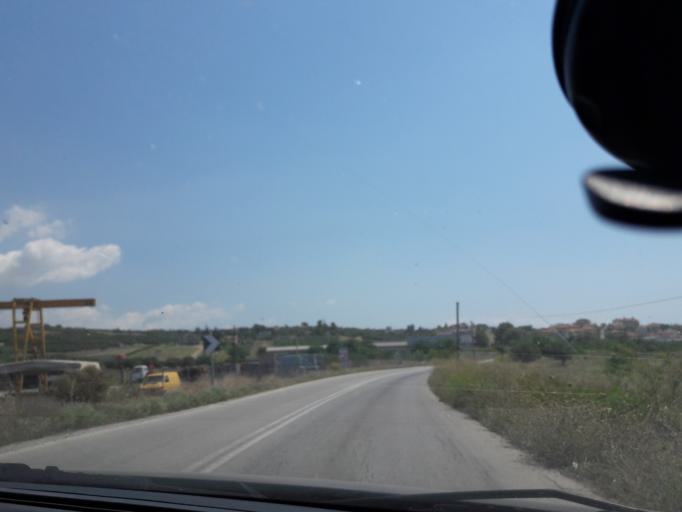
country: GR
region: Central Macedonia
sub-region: Nomos Chalkidikis
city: Nea Kallikrateia
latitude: 40.3275
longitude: 23.0623
